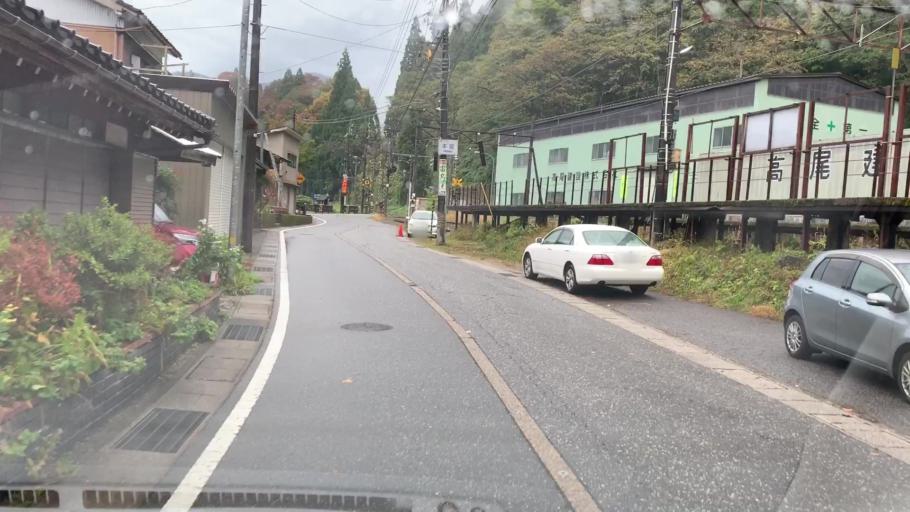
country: JP
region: Toyama
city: Kamiichi
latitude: 36.5750
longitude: 137.3959
